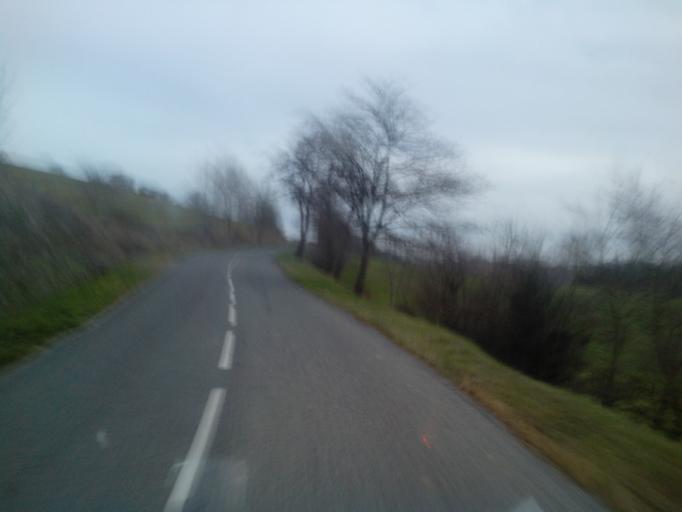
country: FR
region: Languedoc-Roussillon
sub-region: Departement de l'Aude
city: Belpech
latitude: 43.2620
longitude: 1.7491
